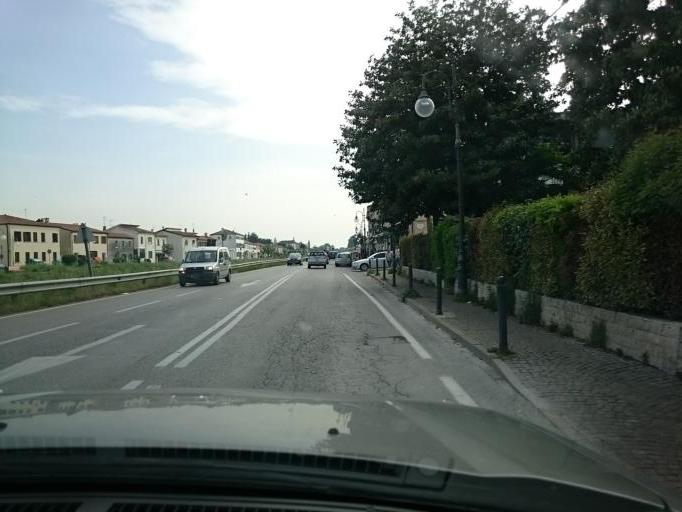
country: IT
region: Veneto
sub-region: Provincia di Venezia
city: Fornase
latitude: 45.4525
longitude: 12.1731
